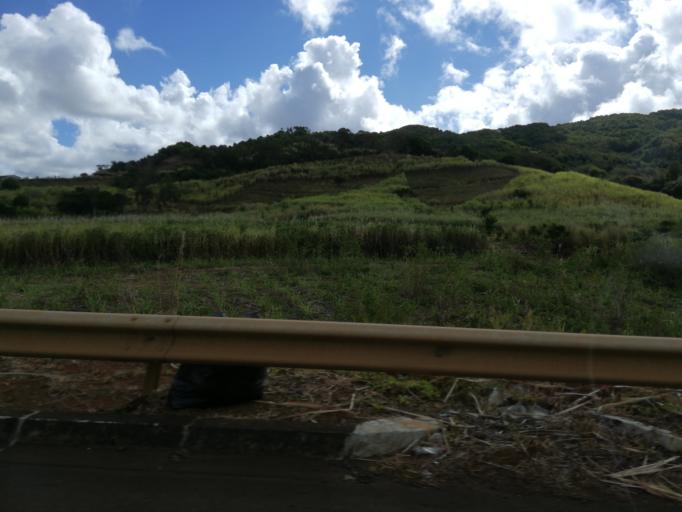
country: MU
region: Grand Port
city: Mahebourg
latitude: -20.3977
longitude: 57.6885
